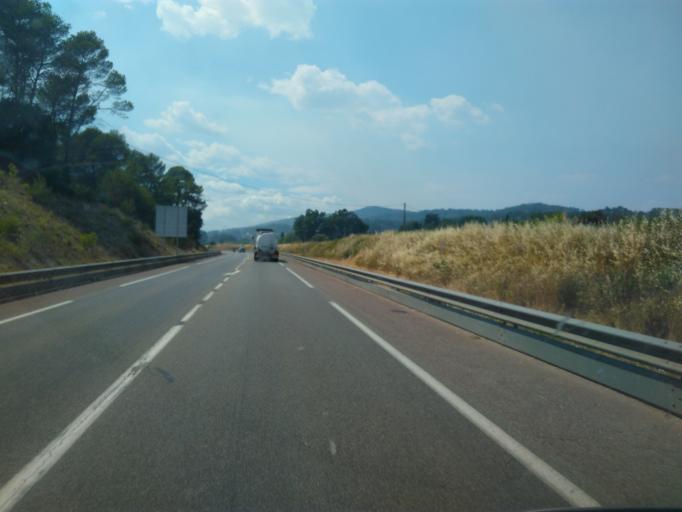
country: FR
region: Provence-Alpes-Cote d'Azur
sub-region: Departement du Var
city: Brignoles
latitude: 43.4161
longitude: 6.0611
